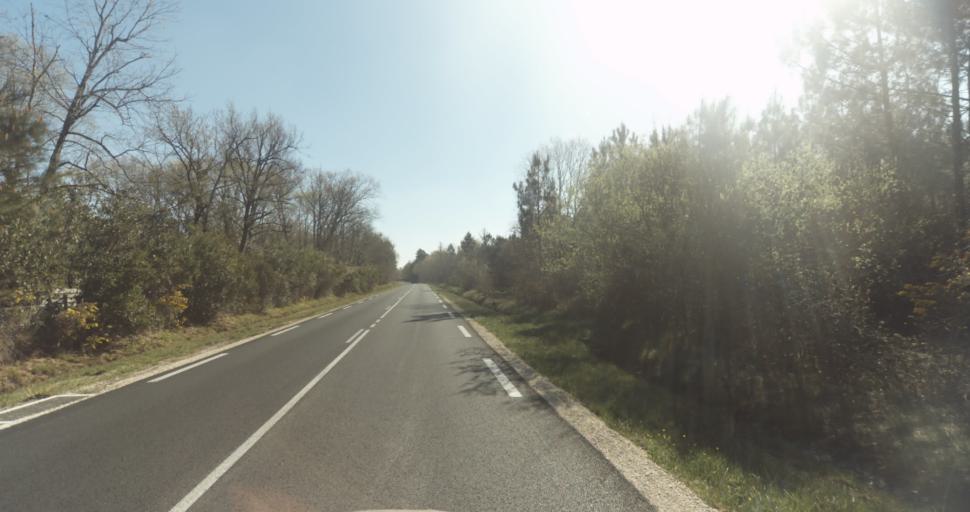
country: FR
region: Aquitaine
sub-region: Departement de la Gironde
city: Martignas-sur-Jalle
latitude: 44.7956
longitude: -0.8474
